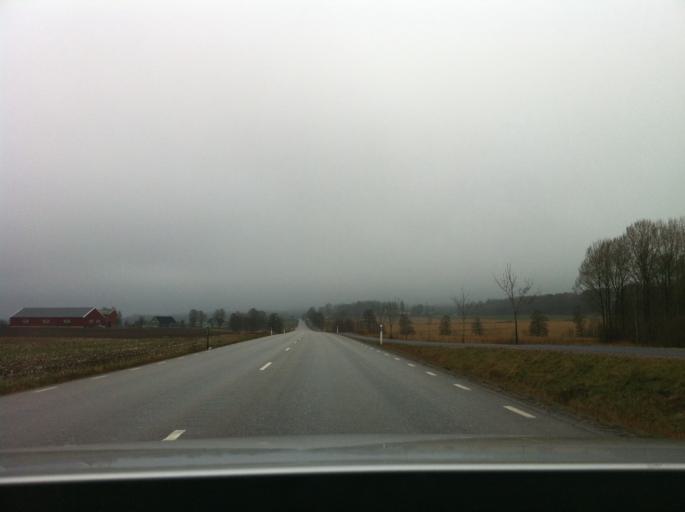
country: SE
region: Vaestra Goetaland
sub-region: Alingsas Kommun
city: Sollebrunn
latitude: 58.1012
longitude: 12.5105
